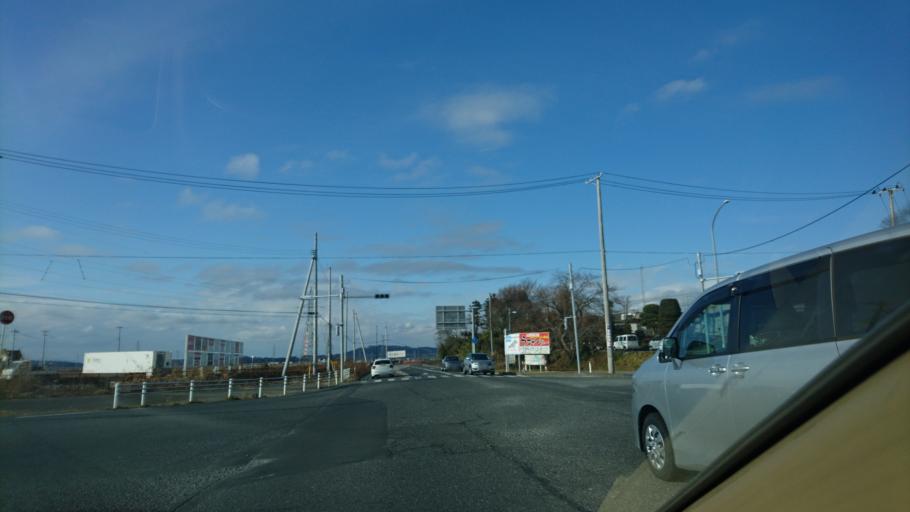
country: JP
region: Miyagi
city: Yamoto
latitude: 38.4599
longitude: 141.2447
